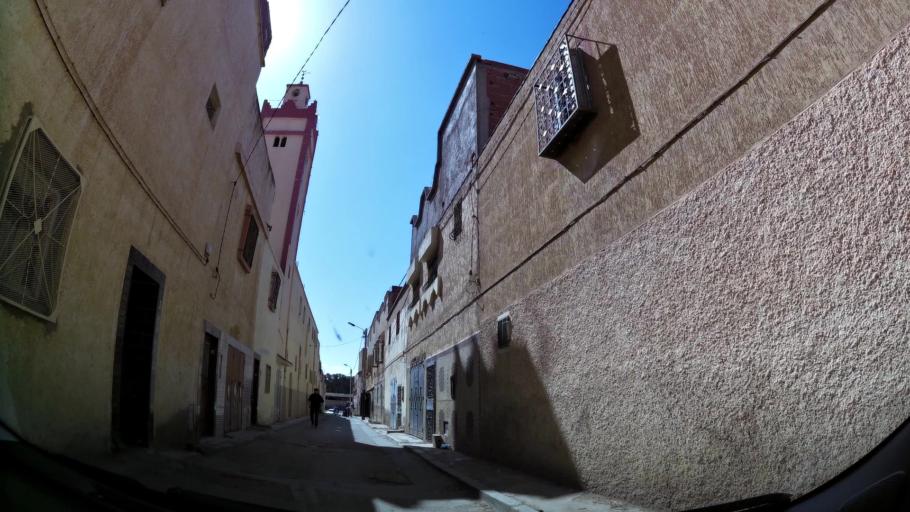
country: MA
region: Oriental
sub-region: Oujda-Angad
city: Oujda
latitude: 34.6832
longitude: -1.9284
